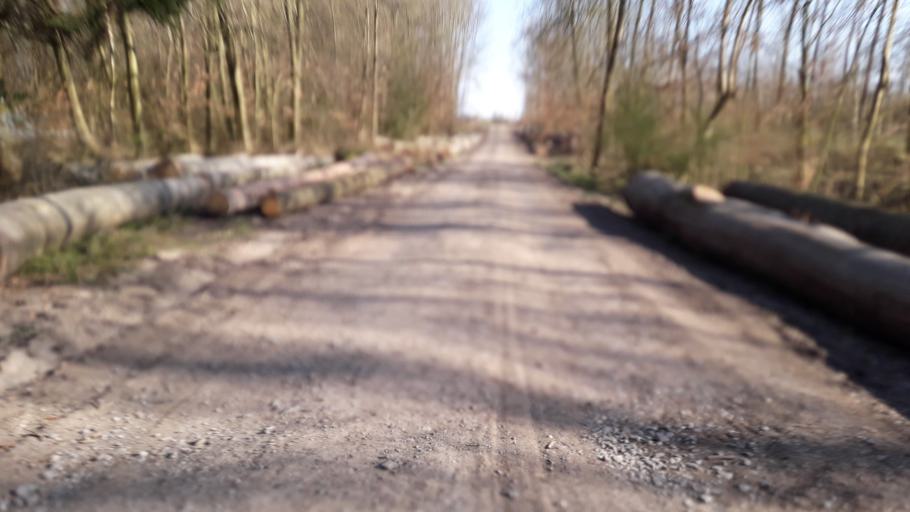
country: DE
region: North Rhine-Westphalia
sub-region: Regierungsbezirk Detmold
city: Salzkotten
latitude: 51.6606
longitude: 8.6701
